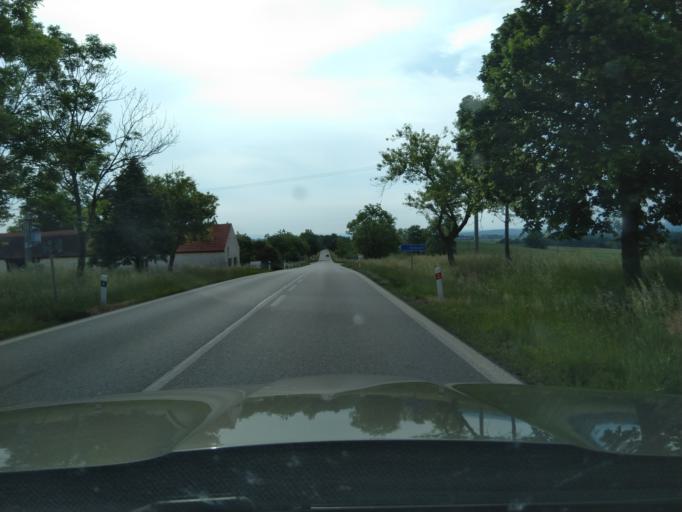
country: CZ
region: Jihocesky
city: Netolice
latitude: 49.0403
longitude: 14.2296
